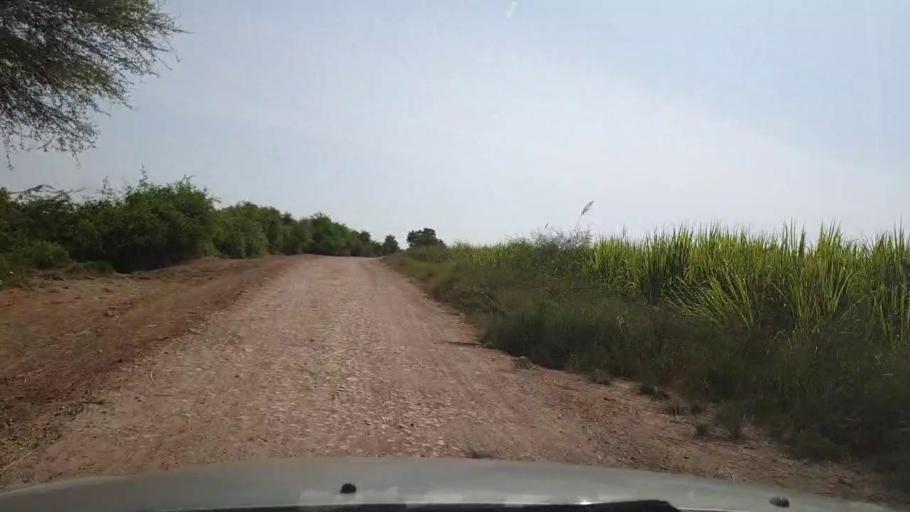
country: PK
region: Sindh
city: Bulri
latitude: 25.0085
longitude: 68.3203
